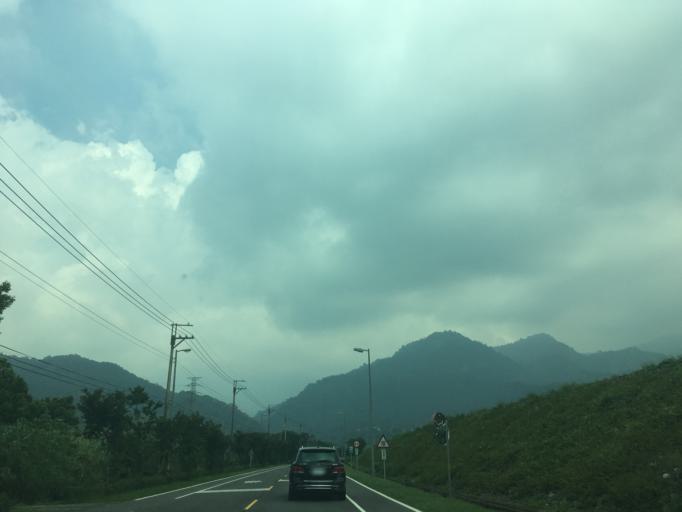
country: TW
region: Taiwan
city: Fengyuan
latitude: 24.2961
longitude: 120.8922
